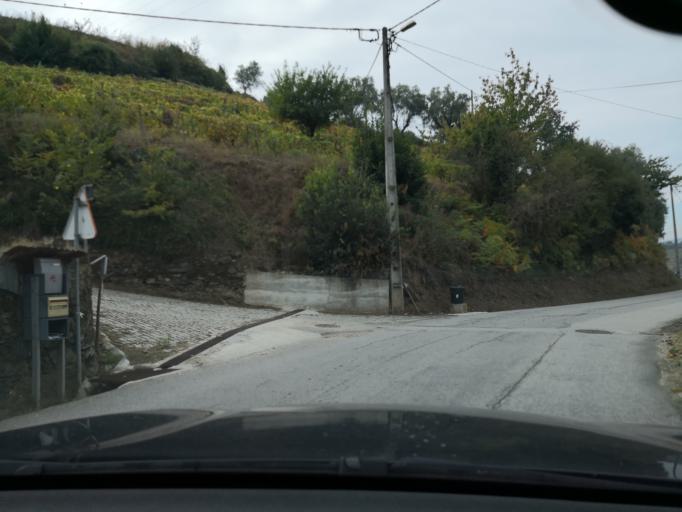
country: PT
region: Vila Real
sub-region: Peso da Regua
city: Peso da Regua
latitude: 41.1767
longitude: -7.7378
